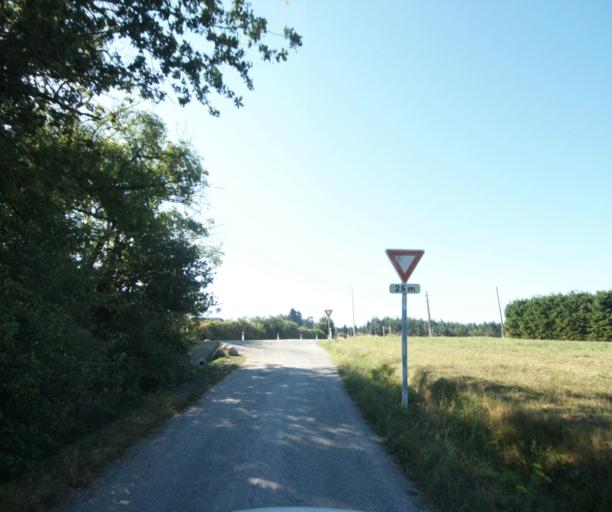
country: FR
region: Lorraine
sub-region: Departement des Vosges
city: Epinal
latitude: 48.1731
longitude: 6.4795
